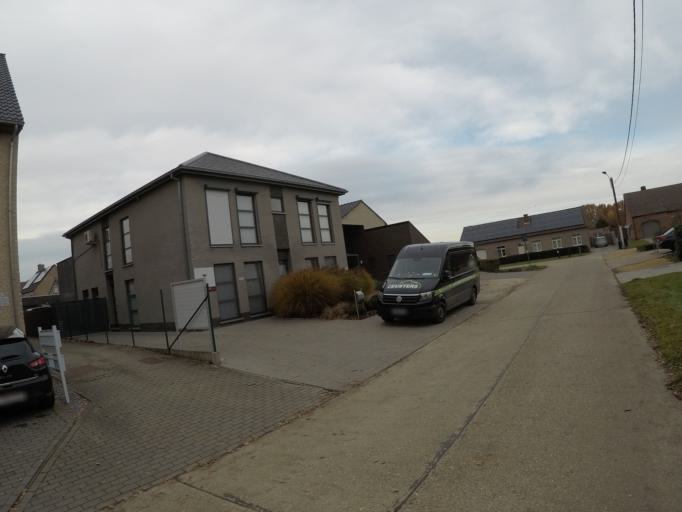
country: BE
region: Flanders
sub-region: Provincie Antwerpen
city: Hulshout
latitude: 51.0773
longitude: 4.7905
